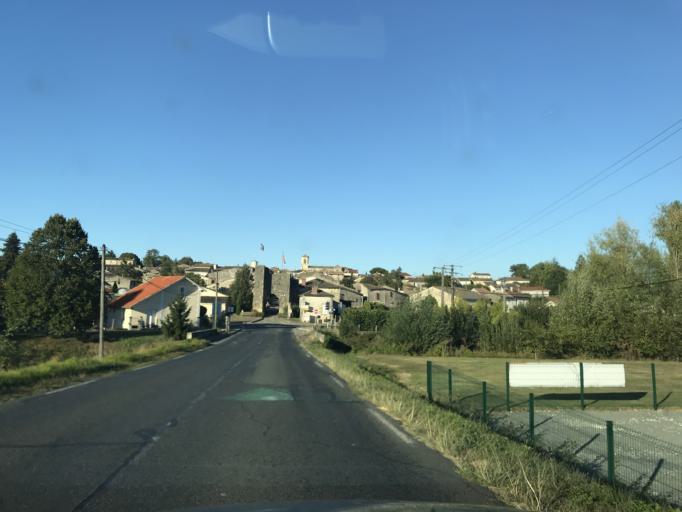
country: FR
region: Aquitaine
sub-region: Departement de la Gironde
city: Sauveterre-de-Guyenne
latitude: 44.6899
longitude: -0.0891
